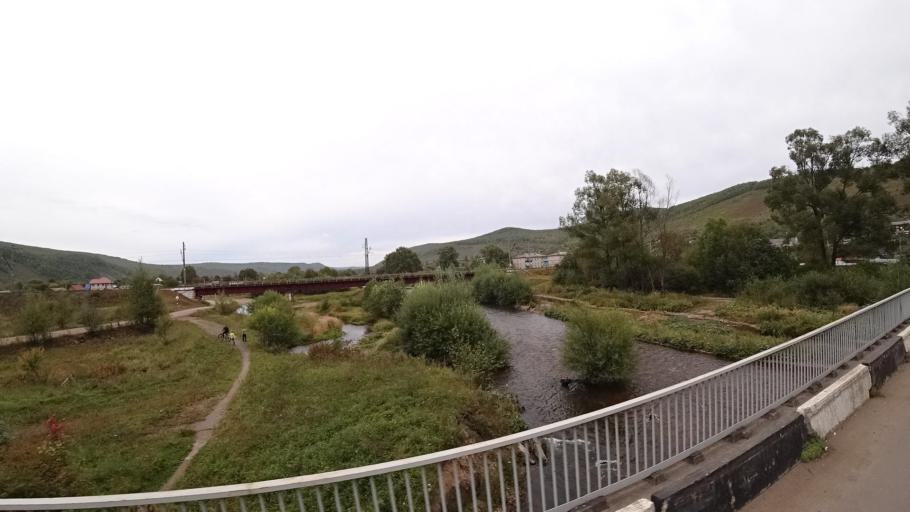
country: RU
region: Jewish Autonomous Oblast
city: Khingansk
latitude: 49.0293
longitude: 131.0510
